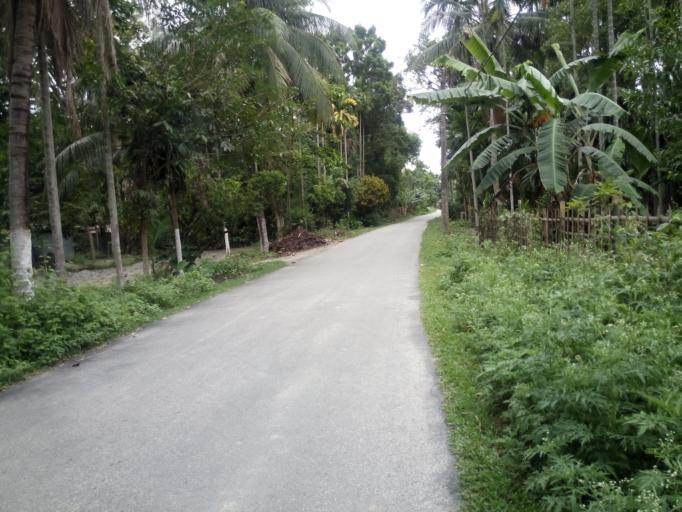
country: IN
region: Assam
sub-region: Udalguri
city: Udalguri
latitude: 26.6910
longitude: 92.1552
